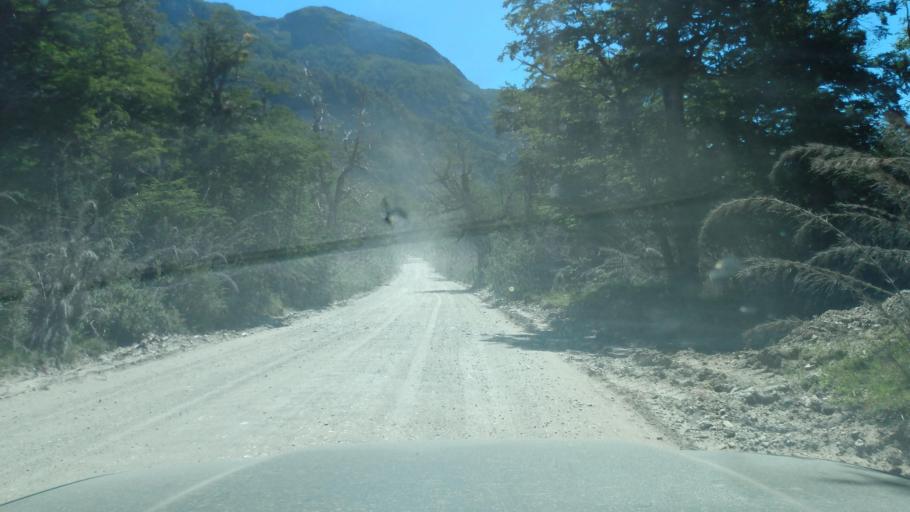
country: AR
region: Neuquen
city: Villa La Angostura
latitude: -40.6207
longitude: -71.5976
